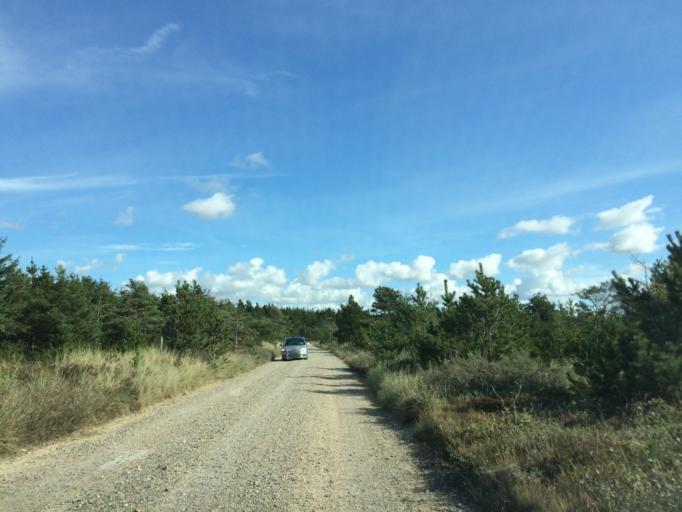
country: DK
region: Central Jutland
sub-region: Holstebro Kommune
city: Ulfborg
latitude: 56.2878
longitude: 8.1413
